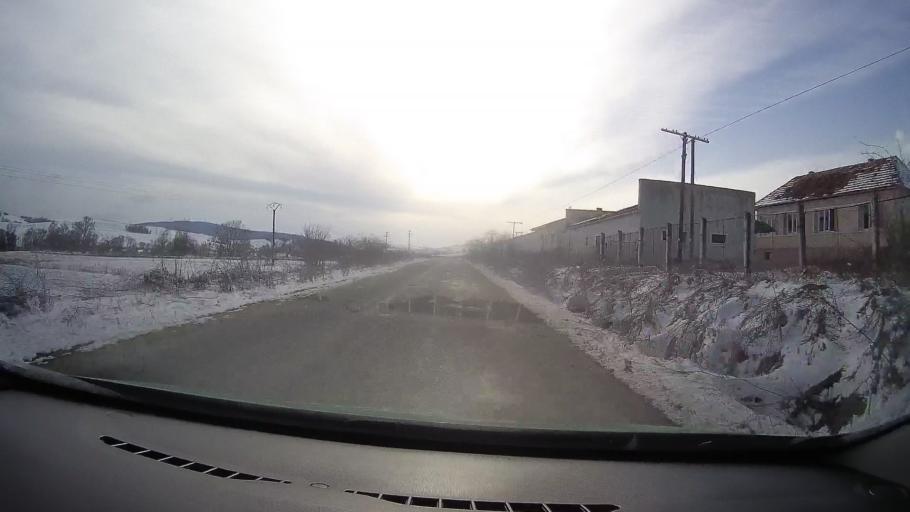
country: RO
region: Sibiu
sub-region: Oras Agnita
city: Ruja
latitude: 46.0123
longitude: 24.6869
